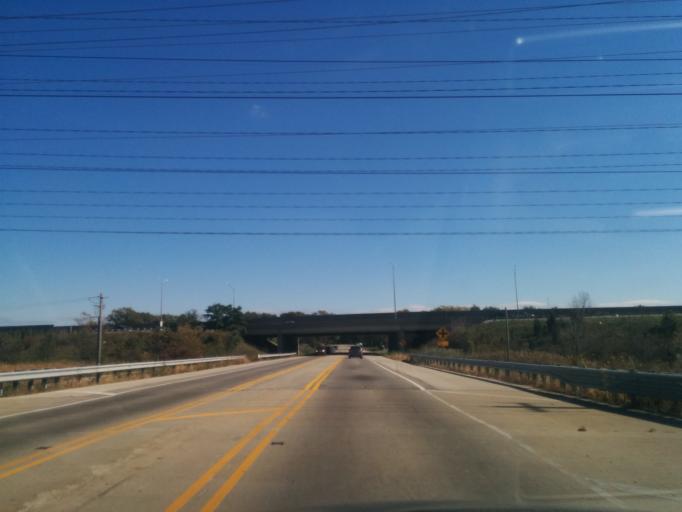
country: US
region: Illinois
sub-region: DuPage County
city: Glen Ellyn
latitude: 41.8655
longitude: -88.0416
